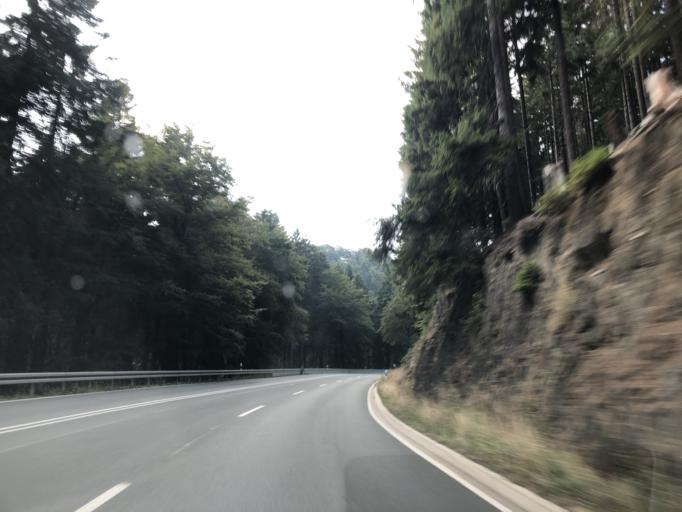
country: DE
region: North Rhine-Westphalia
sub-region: Regierungsbezirk Arnsberg
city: Winterberg
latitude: 51.1869
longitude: 8.5223
